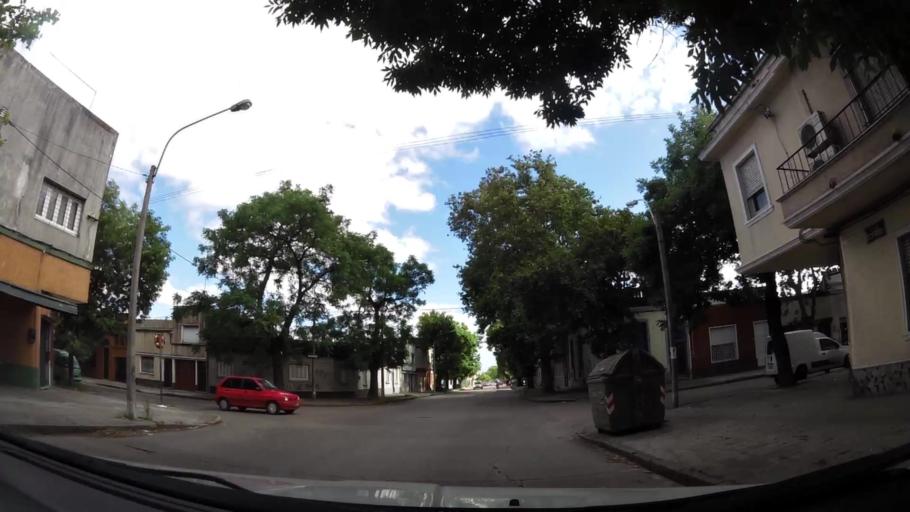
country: UY
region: Montevideo
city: Montevideo
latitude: -34.8731
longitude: -56.1846
